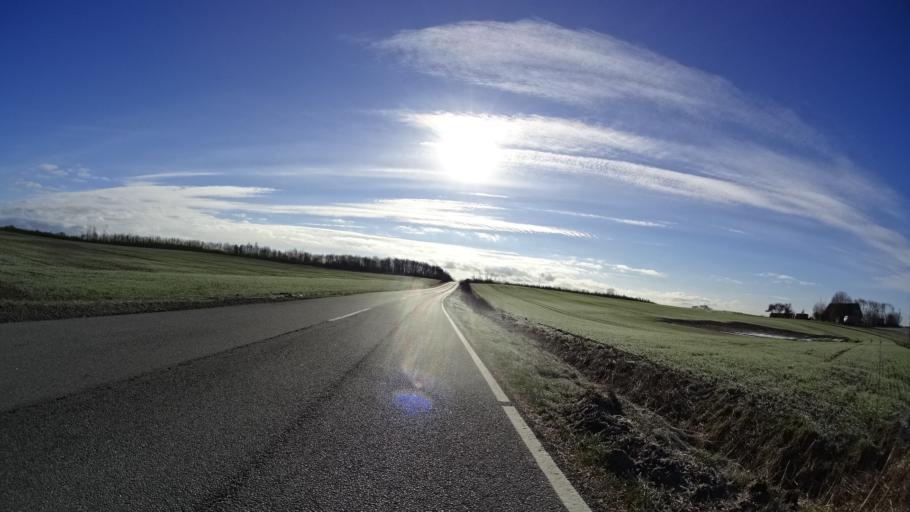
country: DK
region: Central Jutland
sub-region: Arhus Kommune
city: Kolt
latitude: 56.1196
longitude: 10.0671
